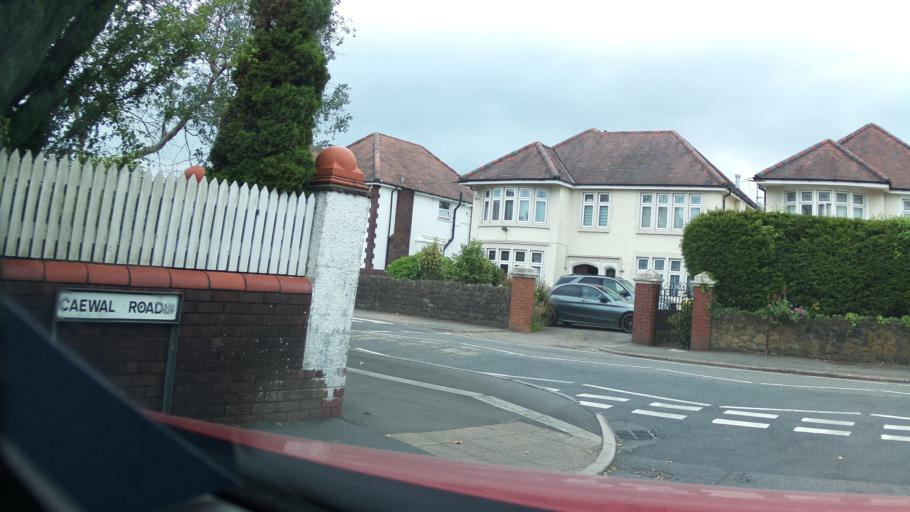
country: GB
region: Wales
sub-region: Cardiff
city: Cardiff
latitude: 51.4893
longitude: -3.2194
